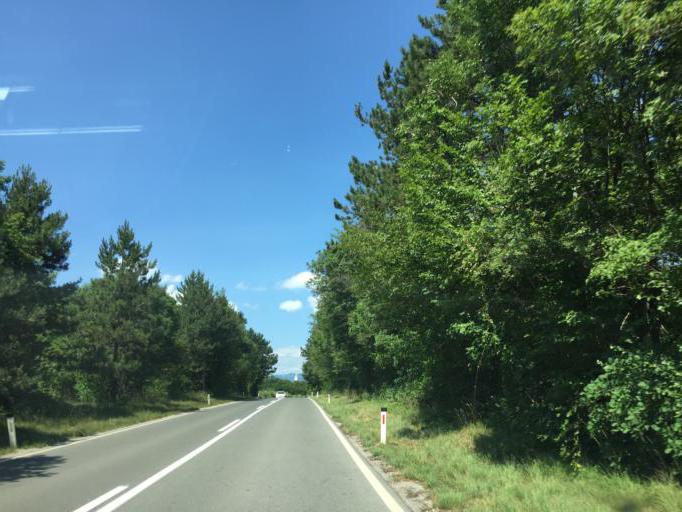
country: SI
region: Sezana
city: Sezana
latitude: 45.7355
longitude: 13.8667
